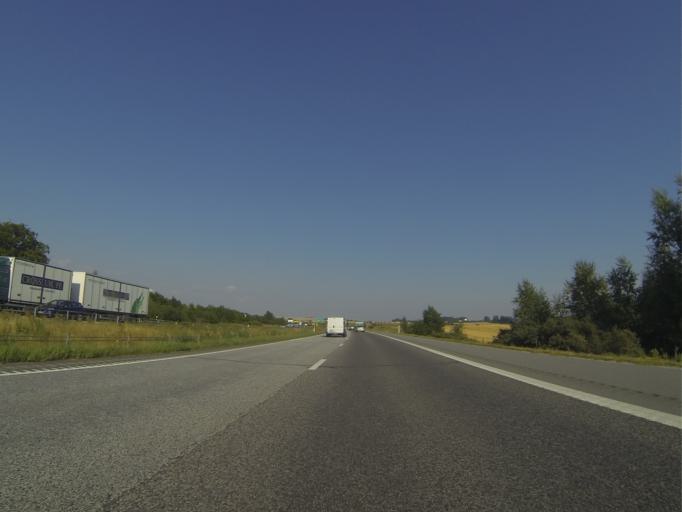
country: SE
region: Skane
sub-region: Malmo
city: Oxie
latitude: 55.5498
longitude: 13.0509
